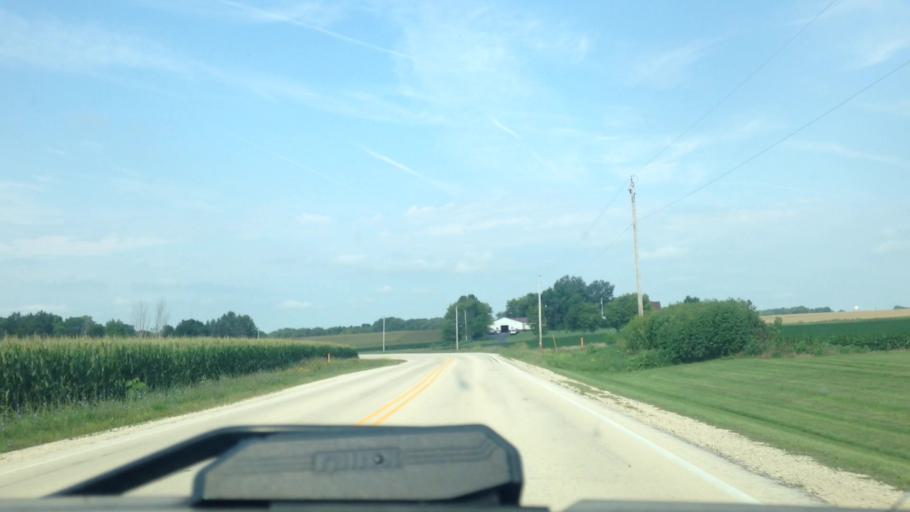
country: US
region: Wisconsin
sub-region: Dodge County
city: Theresa
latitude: 43.5366
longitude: -88.4912
